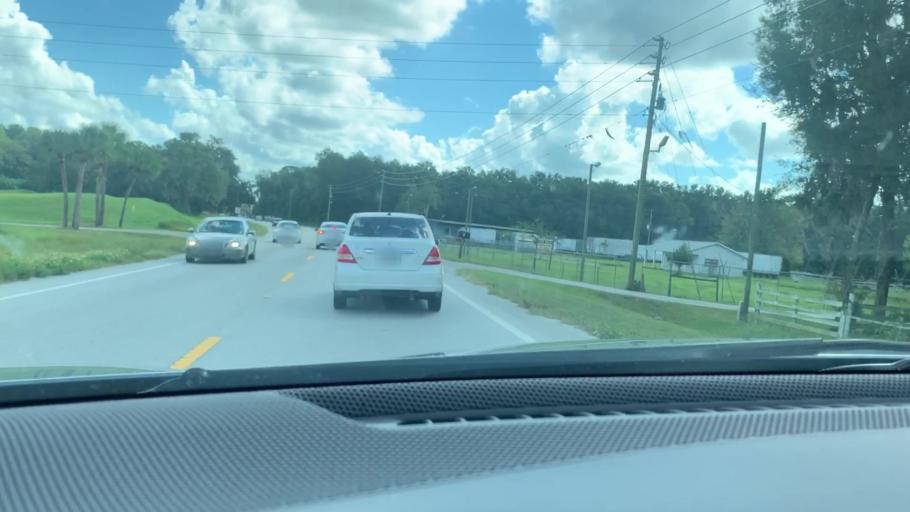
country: US
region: Florida
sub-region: Marion County
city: Ocala
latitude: 29.2670
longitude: -82.1580
